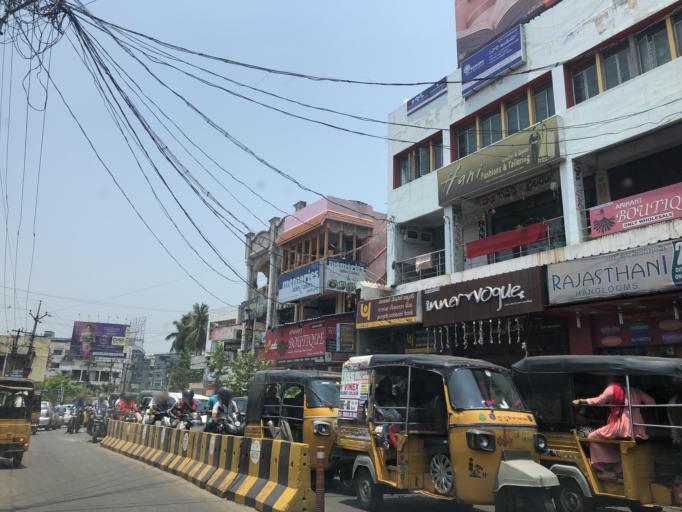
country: IN
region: Andhra Pradesh
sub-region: Vishakhapatnam
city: Yarada
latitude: 17.7139
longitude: 83.3035
